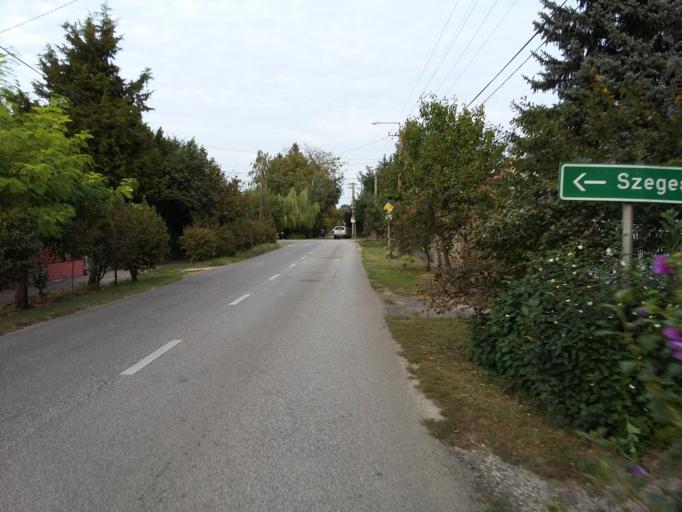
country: HU
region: Csongrad
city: Szeged
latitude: 46.2272
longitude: 20.1155
